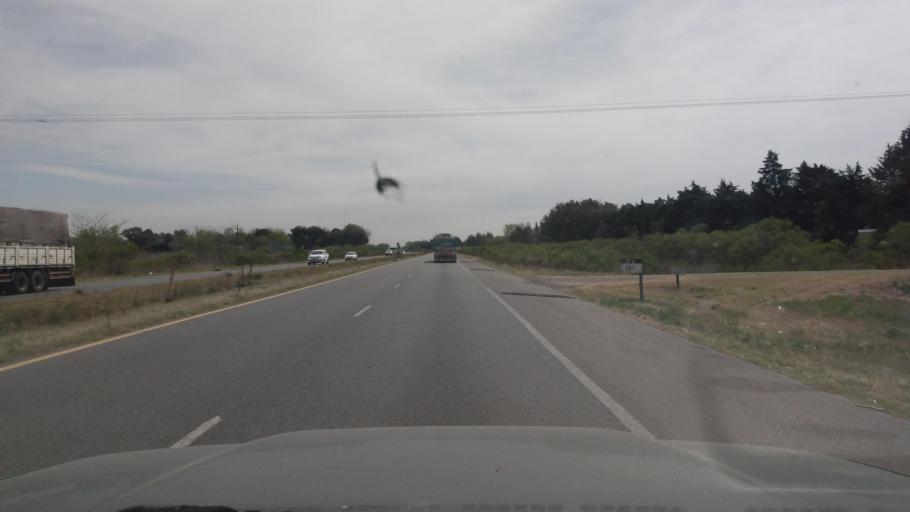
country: AR
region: Buenos Aires
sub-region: Partido de Lujan
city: Lujan
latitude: -34.5078
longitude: -59.0425
